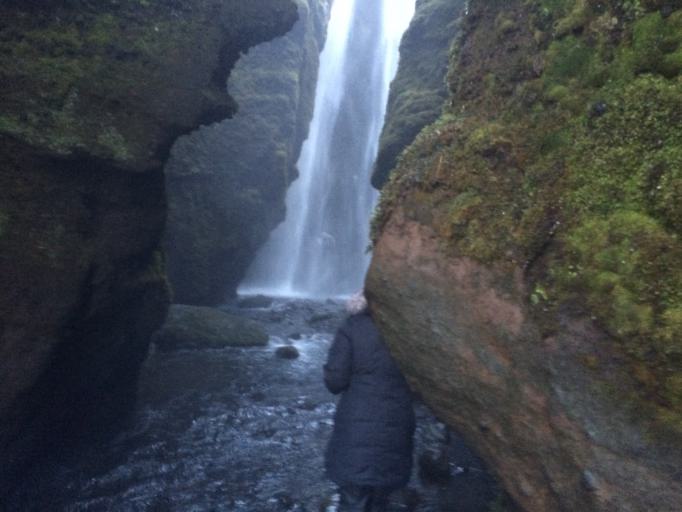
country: IS
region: South
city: Vestmannaeyjar
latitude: 63.6210
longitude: -19.9865
